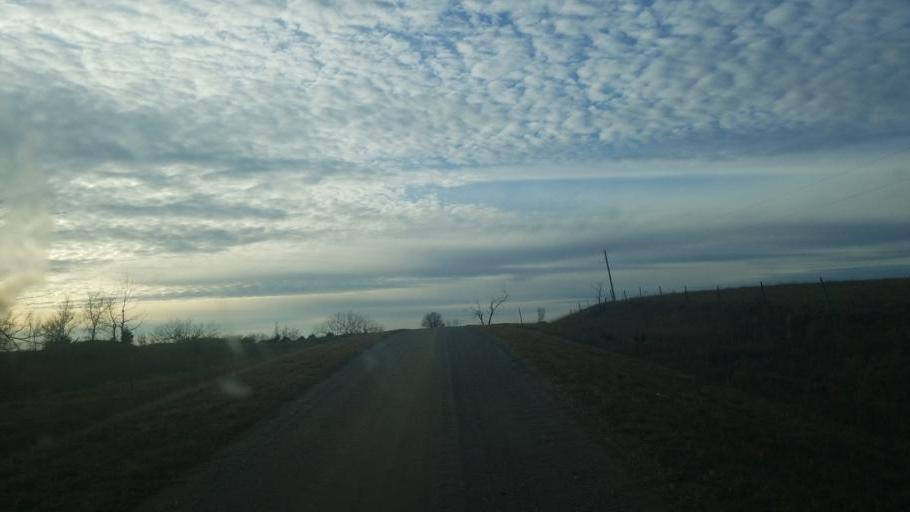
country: US
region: Nebraska
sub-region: Knox County
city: Center
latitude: 42.6981
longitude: -97.8426
